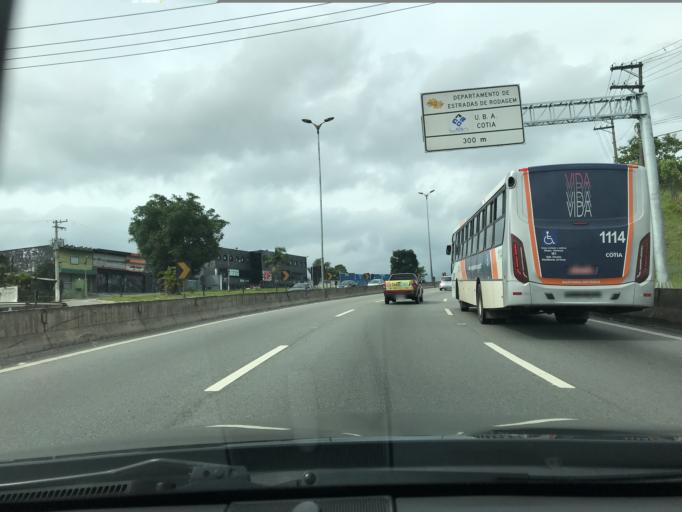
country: BR
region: Sao Paulo
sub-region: Cotia
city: Cotia
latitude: -23.5992
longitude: -46.8817
